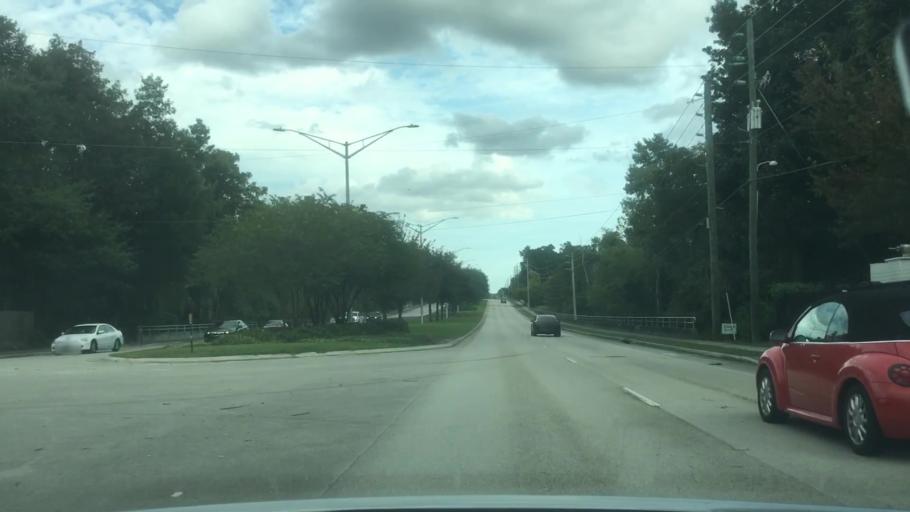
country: US
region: Florida
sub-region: Duval County
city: Jacksonville
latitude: 30.3446
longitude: -81.5322
